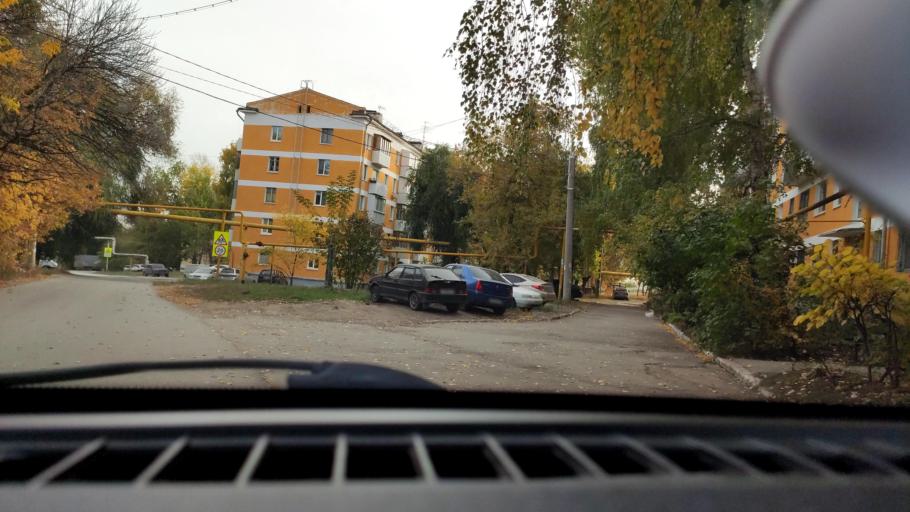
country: RU
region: Samara
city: Petra-Dubrava
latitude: 53.2788
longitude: 50.2694
